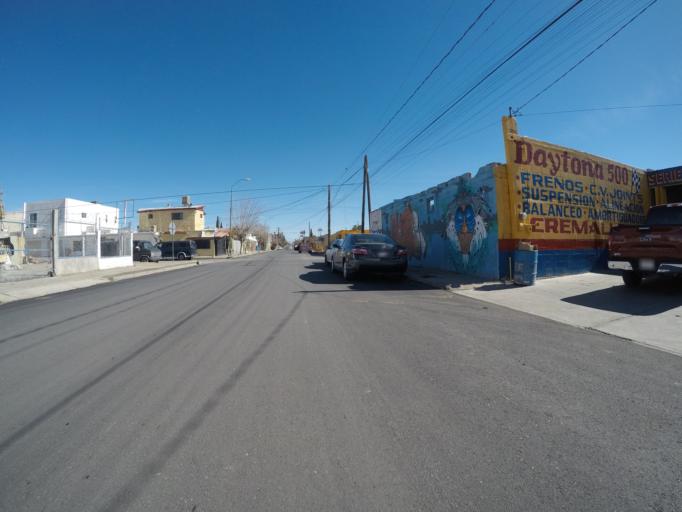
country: MX
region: Chihuahua
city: Ciudad Juarez
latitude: 31.7404
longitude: -106.4636
